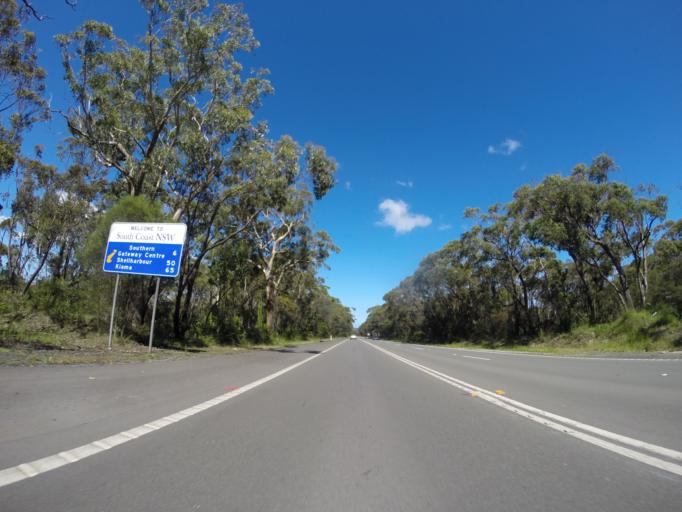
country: AU
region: New South Wales
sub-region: Wollongong
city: Bulli
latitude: -34.2636
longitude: 150.8842
